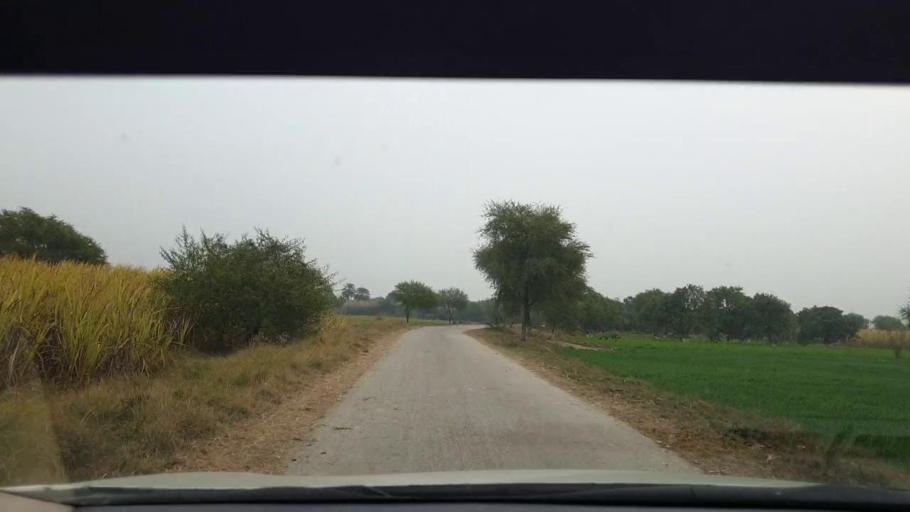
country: PK
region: Sindh
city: Berani
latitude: 25.8574
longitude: 68.8021
